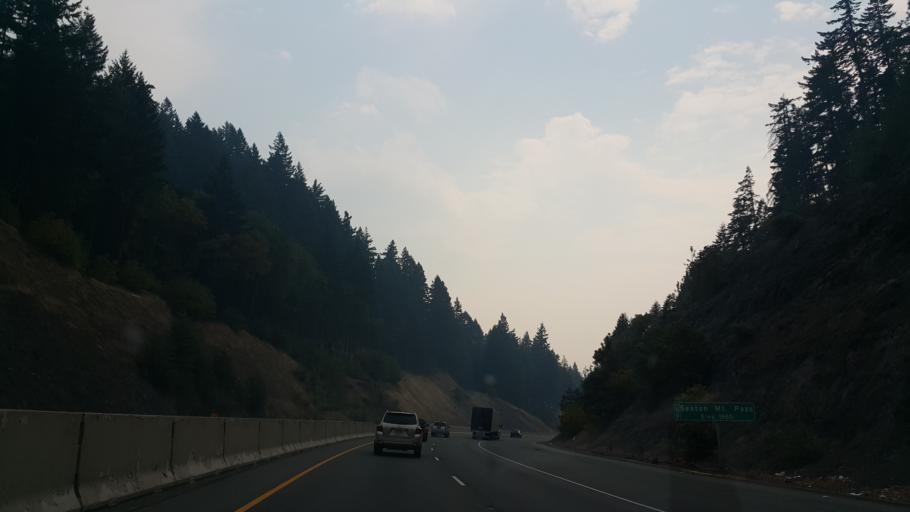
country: US
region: Oregon
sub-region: Josephine County
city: Merlin
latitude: 42.6014
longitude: -123.3833
